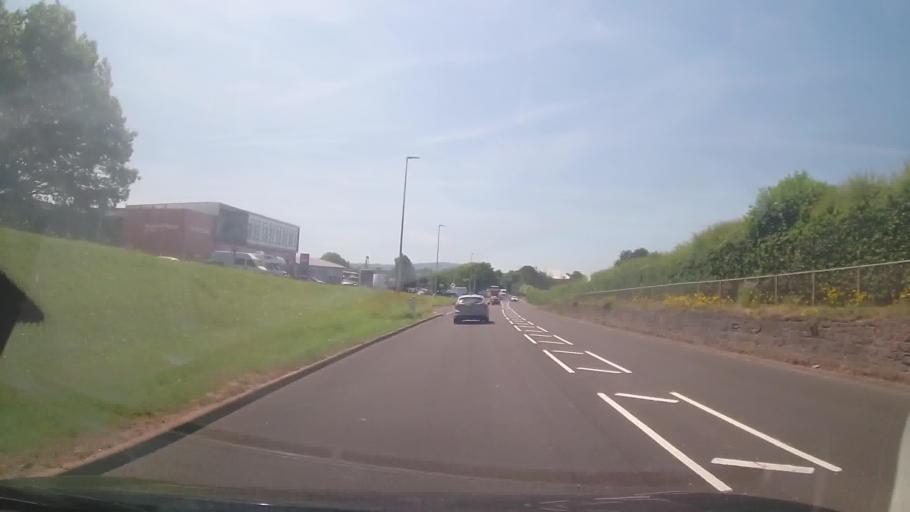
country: GB
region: England
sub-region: Herefordshire
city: Hereford
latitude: 52.0733
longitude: -2.7220
